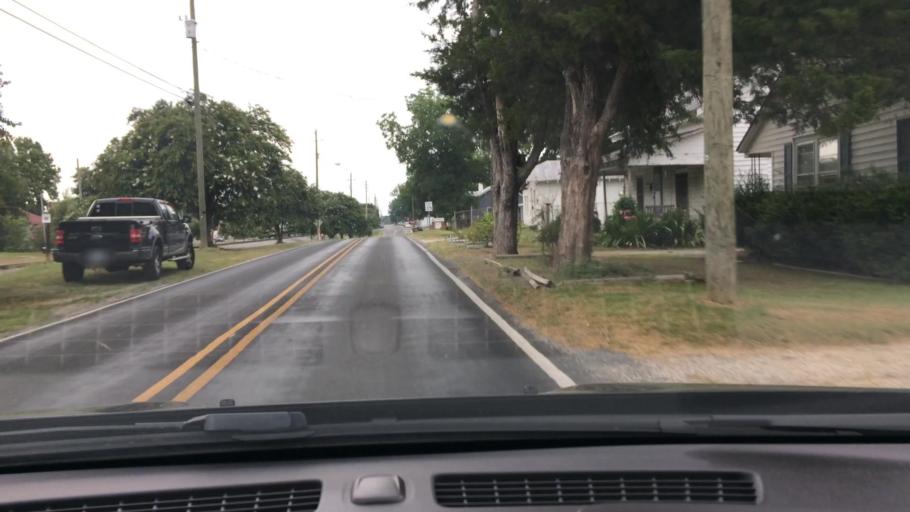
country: US
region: North Carolina
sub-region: Pitt County
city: Ayden
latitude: 35.4684
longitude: -77.4162
